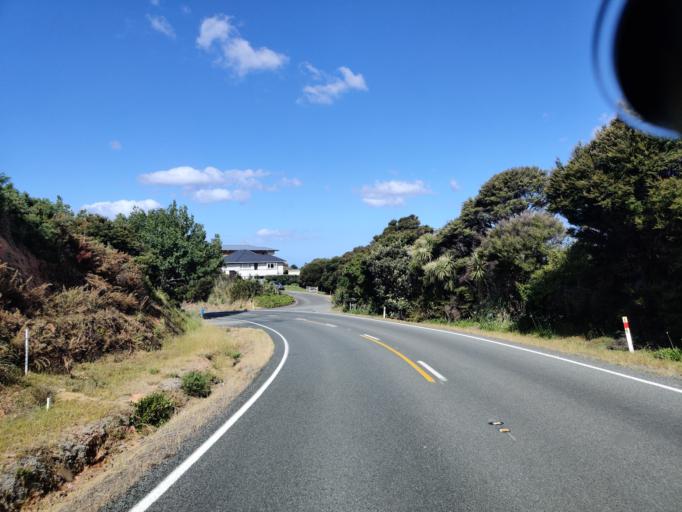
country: NZ
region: Northland
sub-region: Whangarei
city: Ngunguru
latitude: -35.6173
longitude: 174.5182
